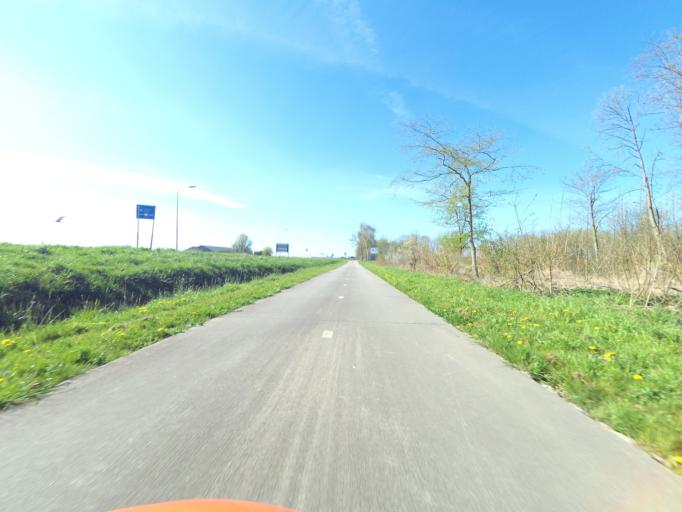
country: NL
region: Flevoland
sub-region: Gemeente Lelystad
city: Lelystad
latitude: 52.4547
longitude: 5.5288
